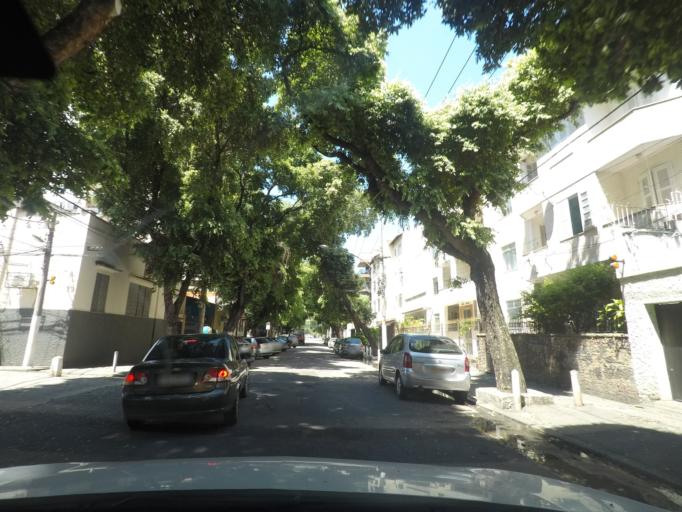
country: BR
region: Rio de Janeiro
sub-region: Rio De Janeiro
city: Rio de Janeiro
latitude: -22.9170
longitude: -43.2361
